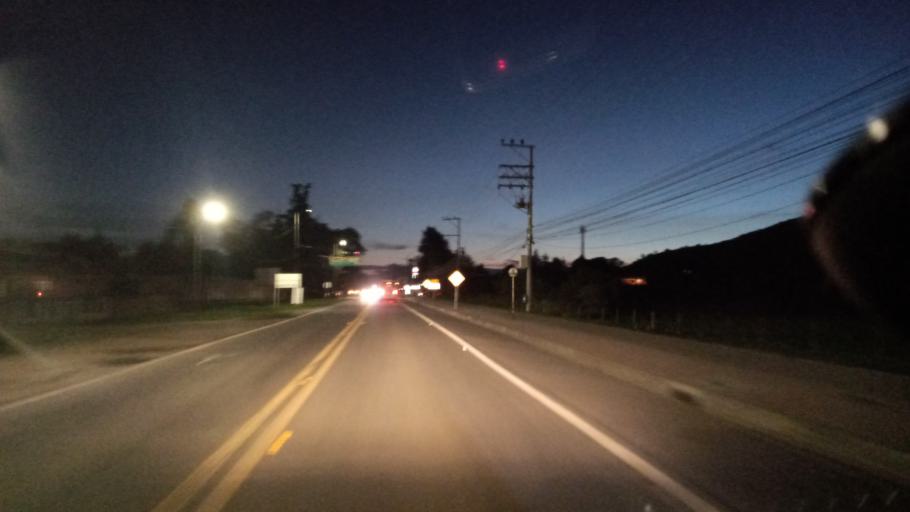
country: CO
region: Cundinamarca
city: Cota
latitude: 4.8009
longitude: -74.1095
